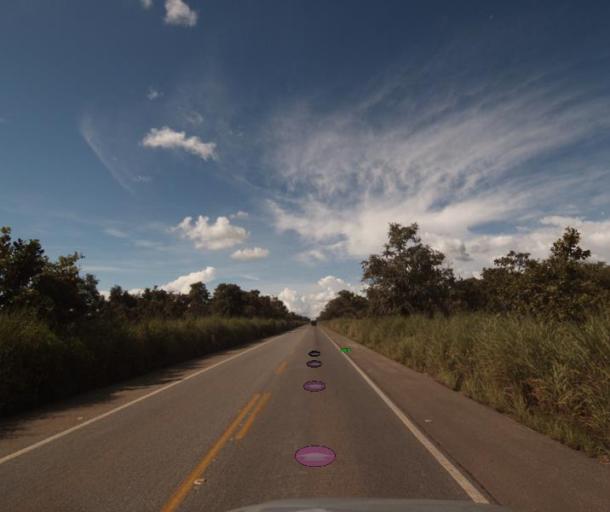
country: BR
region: Goias
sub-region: Porangatu
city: Porangatu
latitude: -13.0844
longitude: -49.1913
